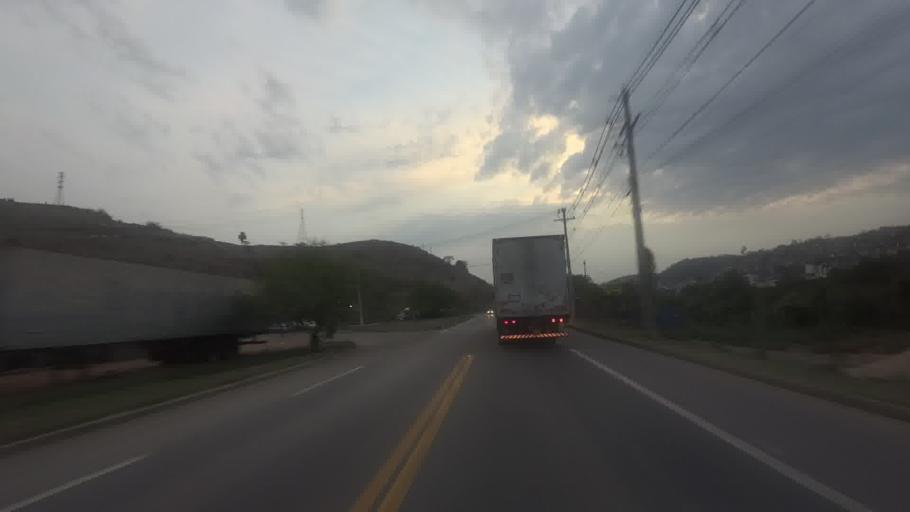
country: BR
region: Minas Gerais
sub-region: Alem Paraiba
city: Alem Paraiba
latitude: -21.8839
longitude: -42.6910
